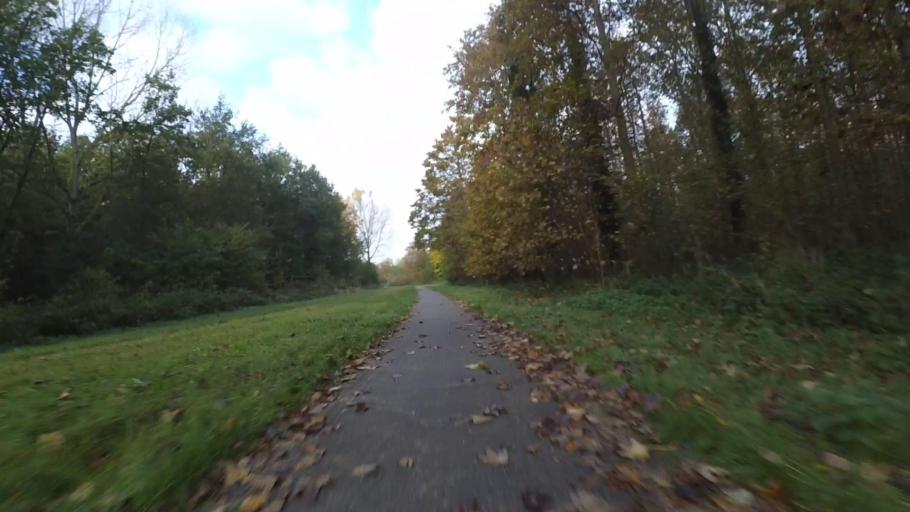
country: NL
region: North Holland
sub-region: Gemeente Huizen
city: Huizen
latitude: 52.3253
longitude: 5.2963
